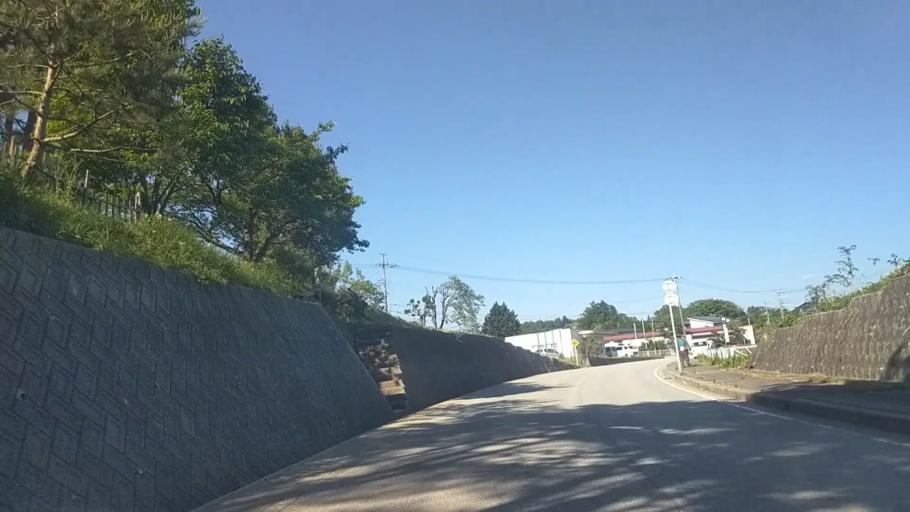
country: JP
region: Nagano
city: Chino
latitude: 35.8615
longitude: 138.2982
